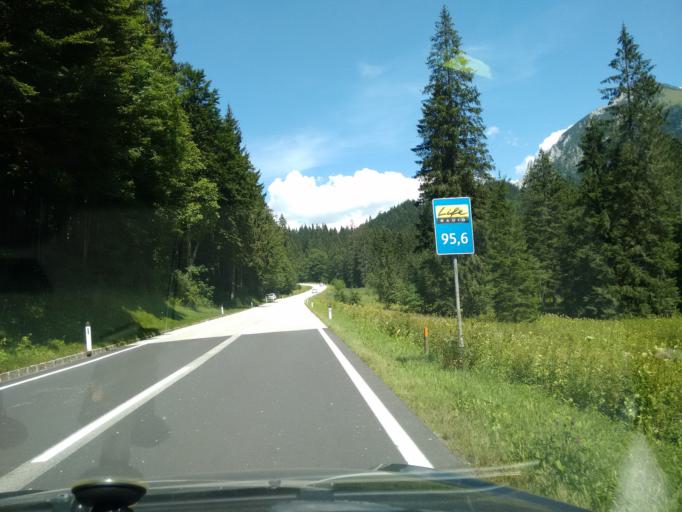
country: AT
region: Styria
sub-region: Politischer Bezirk Liezen
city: Ardning
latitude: 47.6160
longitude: 14.2938
